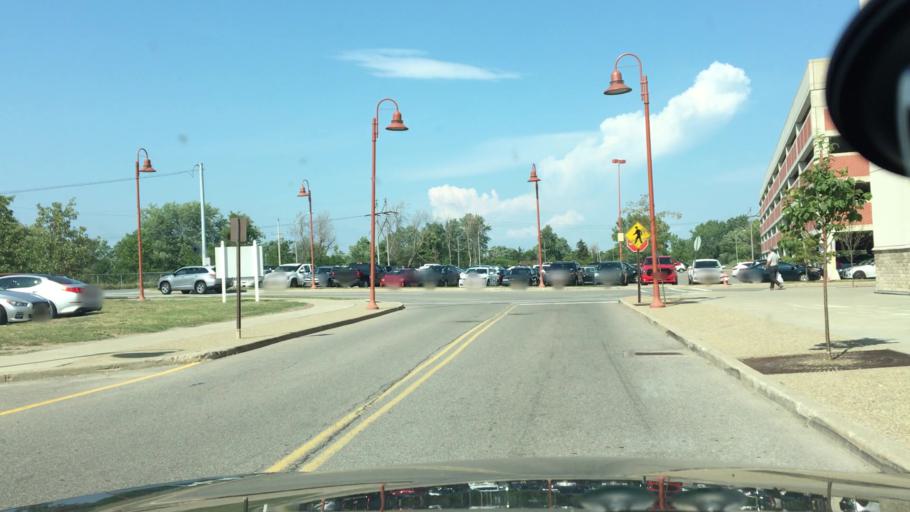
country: US
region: New York
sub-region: Erie County
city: Cheektowaga
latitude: 42.9156
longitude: -78.7625
